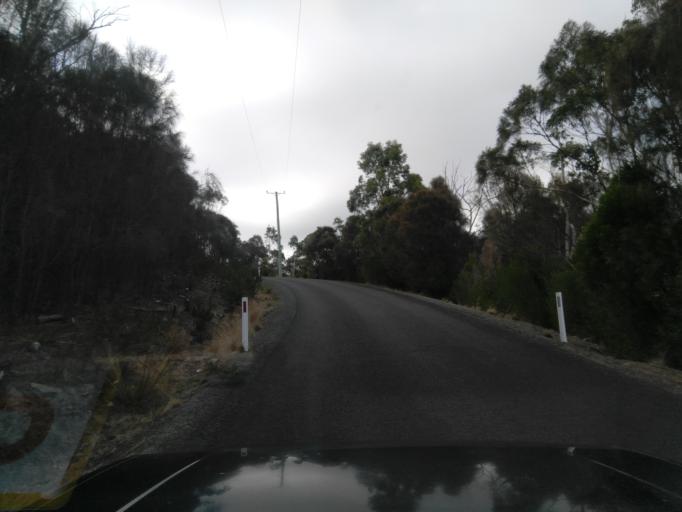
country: AU
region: Tasmania
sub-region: Kingborough
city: Kingston
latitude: -42.9463
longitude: 147.3132
